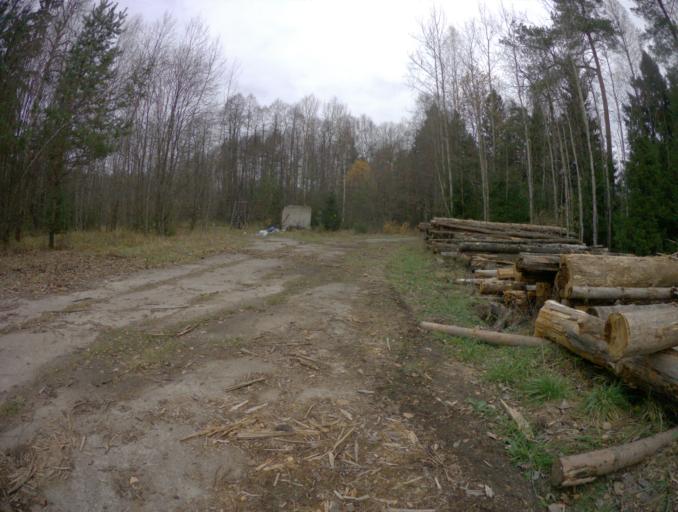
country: RU
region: Vladimir
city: Krasnyy Oktyabr'
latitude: 56.0145
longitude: 38.8517
